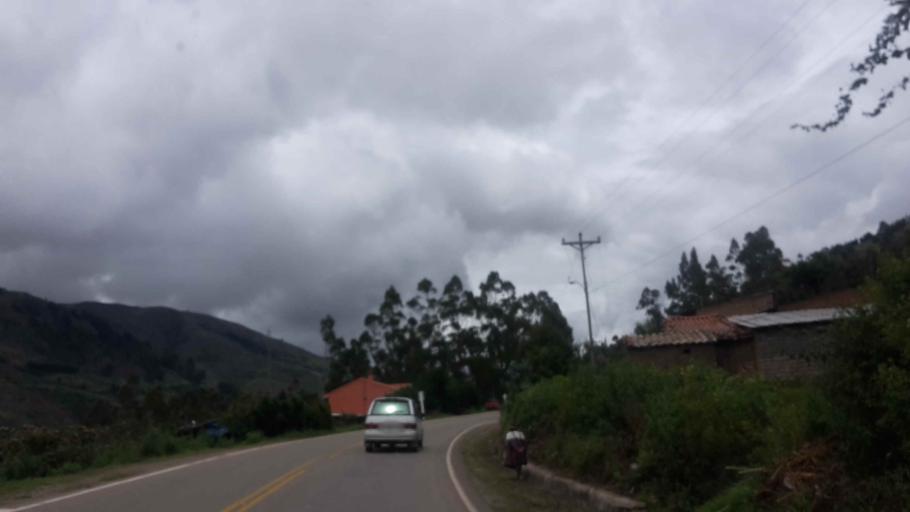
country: BO
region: Cochabamba
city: Totora
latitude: -17.5080
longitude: -65.4053
